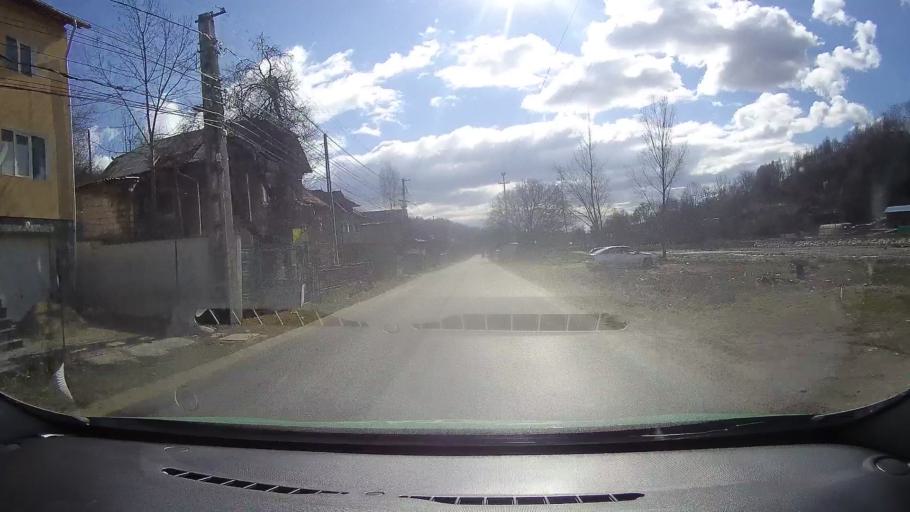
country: RO
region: Dambovita
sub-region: Comuna Runcu
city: Badeni
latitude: 45.1531
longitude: 25.4003
